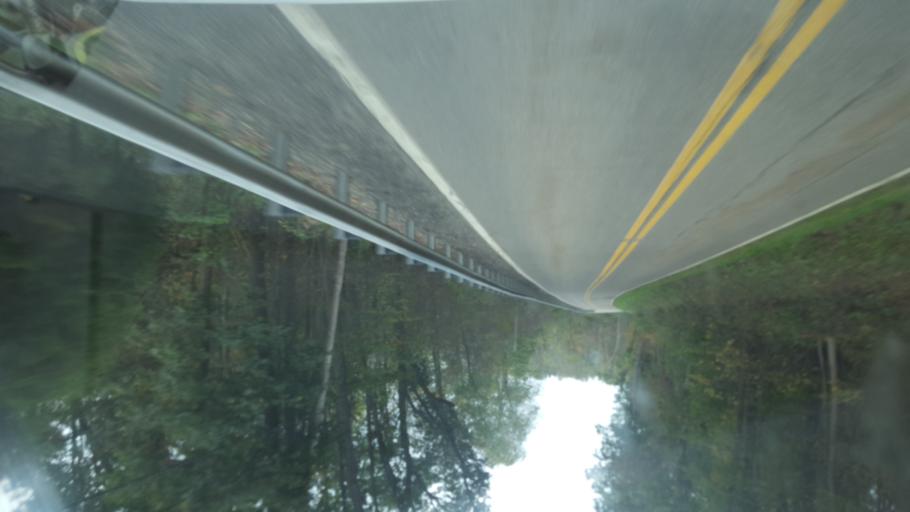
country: US
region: Ohio
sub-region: Knox County
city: Danville
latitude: 40.5216
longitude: -82.1209
